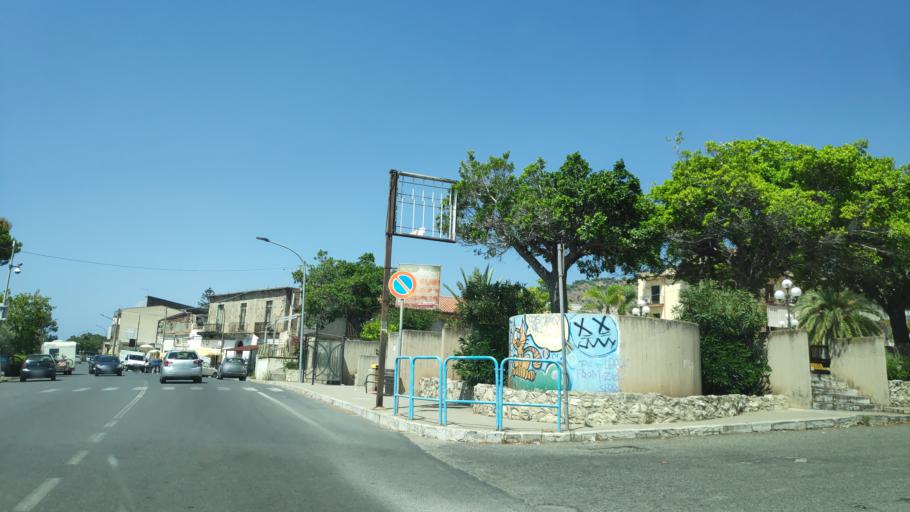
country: IT
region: Calabria
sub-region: Provincia di Reggio Calabria
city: Palizzi Marina
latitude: 37.9191
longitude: 15.9869
